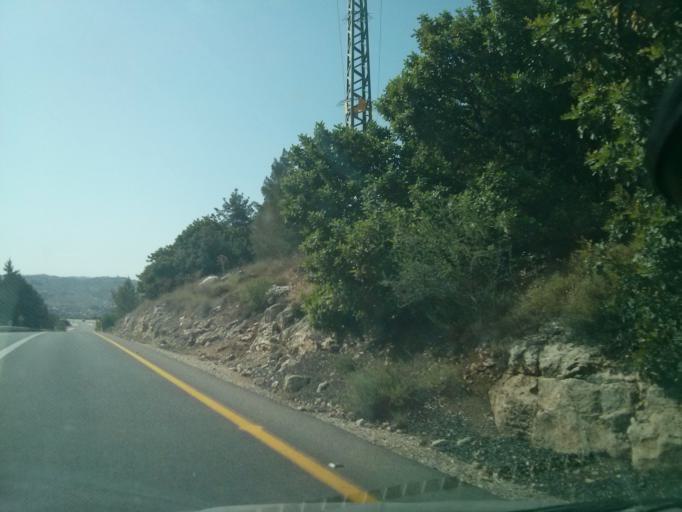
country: PS
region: West Bank
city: Surif
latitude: 31.6740
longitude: 35.0476
